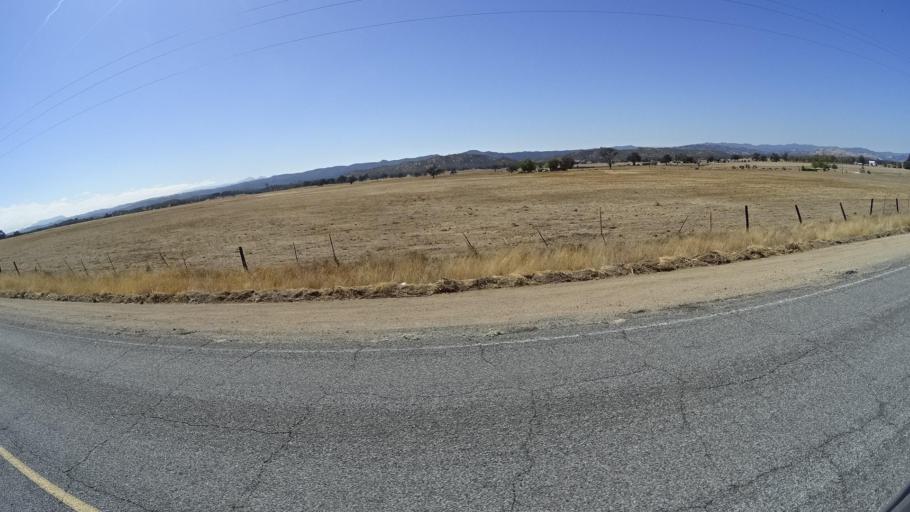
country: US
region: California
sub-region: San Luis Obispo County
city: Lake Nacimiento
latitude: 35.9354
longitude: -121.0607
